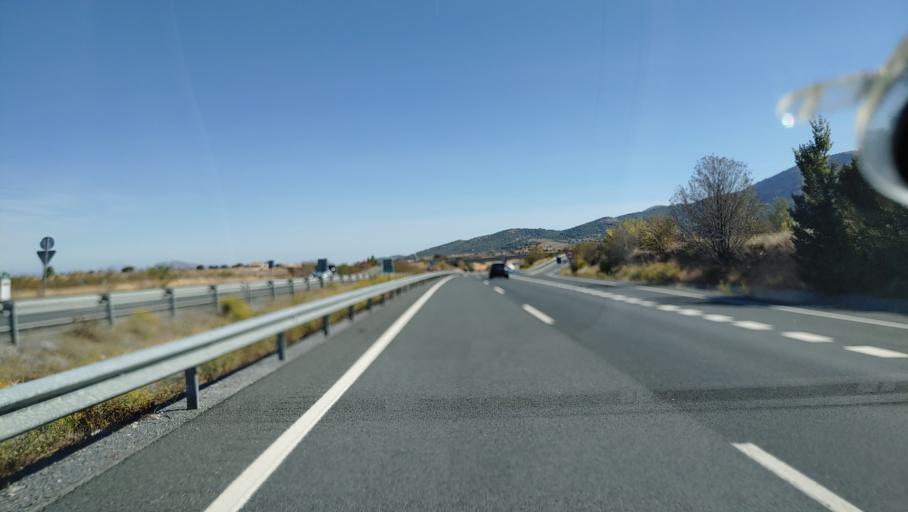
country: ES
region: Andalusia
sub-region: Provincia de Granada
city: Gor
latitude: 37.3975
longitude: -2.9536
